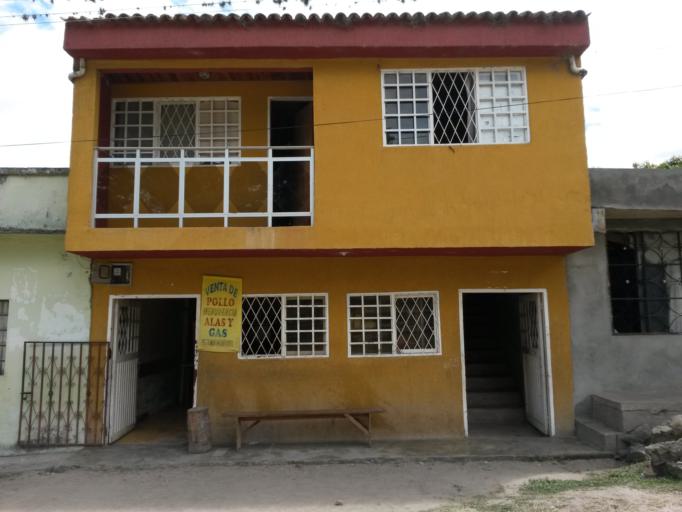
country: CO
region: Cauca
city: Inza
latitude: 2.5276
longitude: -75.9568
